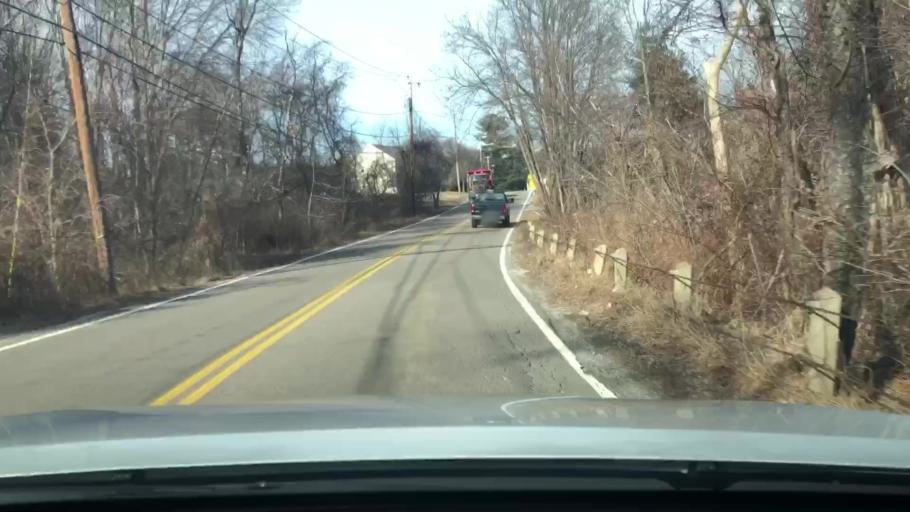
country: US
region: Massachusetts
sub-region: Worcester County
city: Blackstone
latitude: 42.0596
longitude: -71.5263
